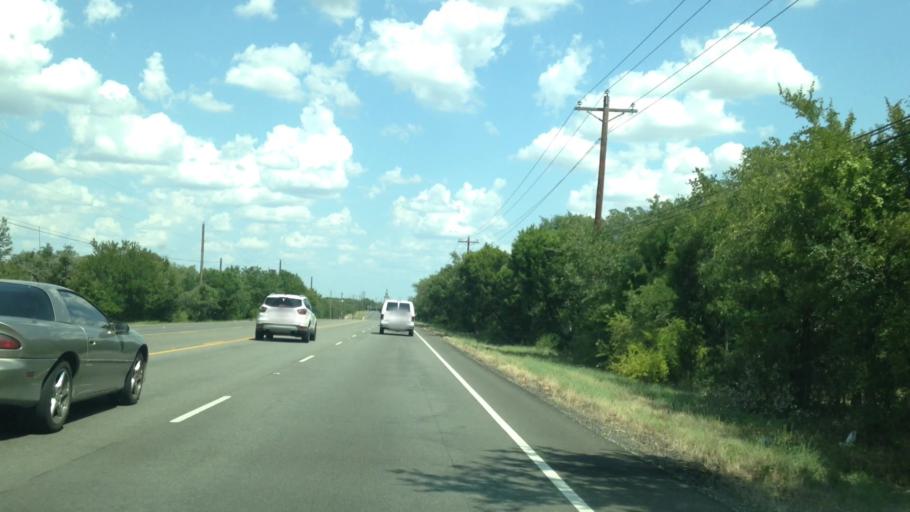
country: US
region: Texas
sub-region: Williamson County
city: Georgetown
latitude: 30.6338
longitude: -97.7207
